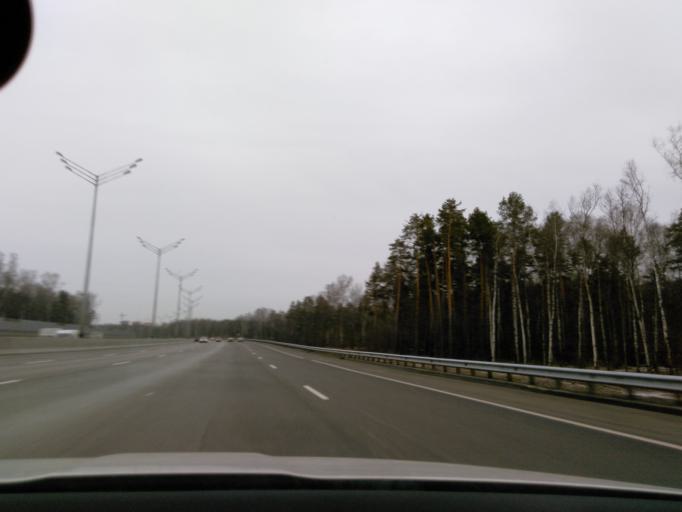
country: RU
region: Moscow
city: Khimki
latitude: 55.9226
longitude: 37.4550
